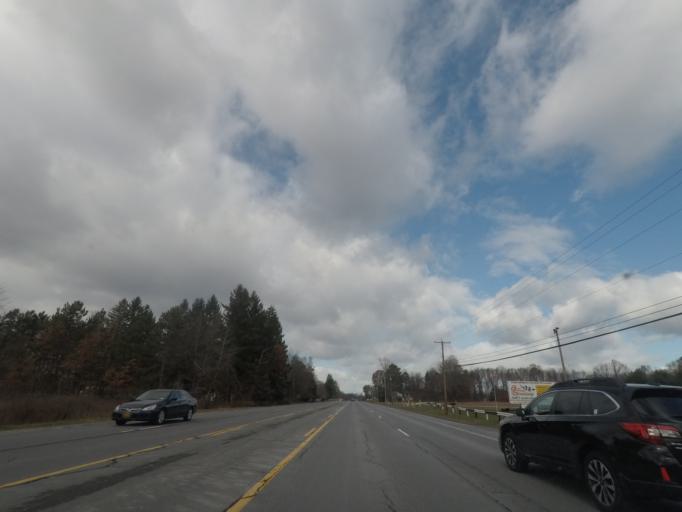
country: US
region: New York
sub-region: Saratoga County
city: Ballston Spa
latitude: 42.9885
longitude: -73.7881
